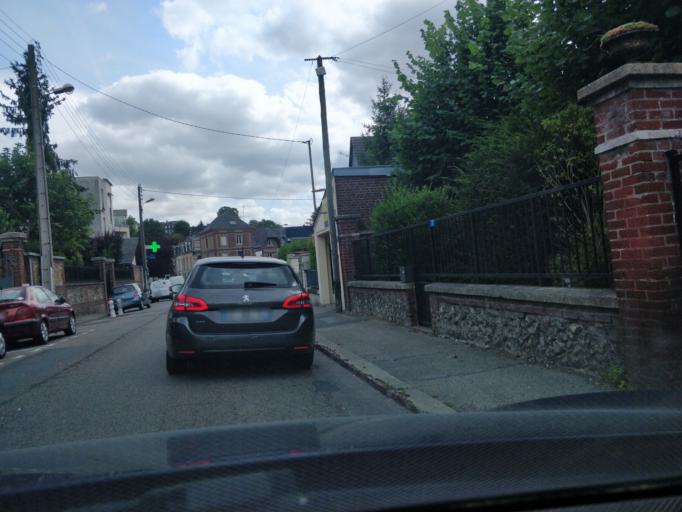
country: FR
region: Haute-Normandie
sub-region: Departement de la Seine-Maritime
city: Mont-Saint-Aignan
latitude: 49.4574
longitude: 1.0947
